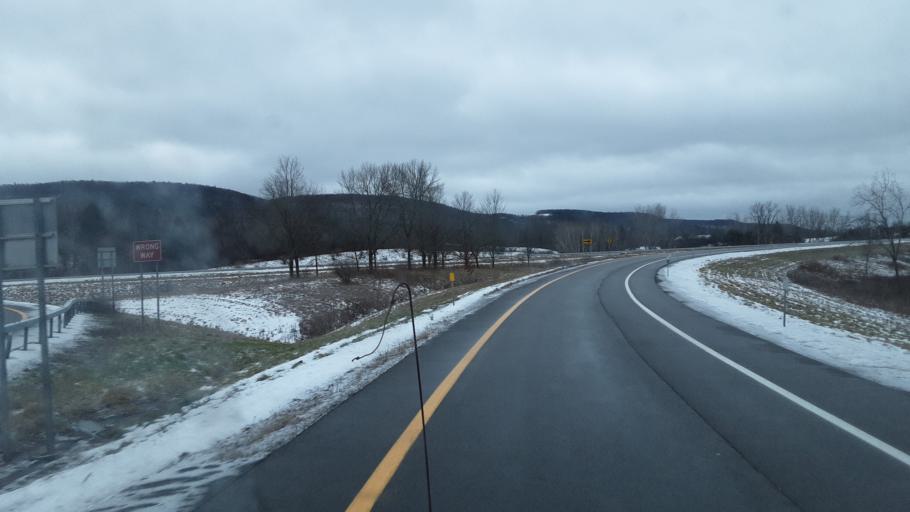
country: US
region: New York
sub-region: Steuben County
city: Hornell
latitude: 42.3240
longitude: -77.7441
